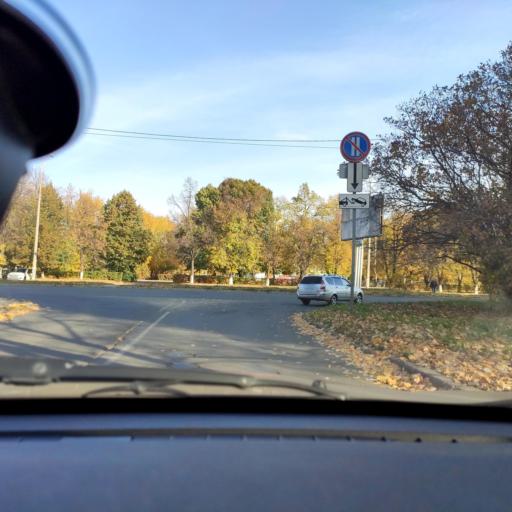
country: RU
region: Samara
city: Tol'yatti
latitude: 53.5154
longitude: 49.2680
